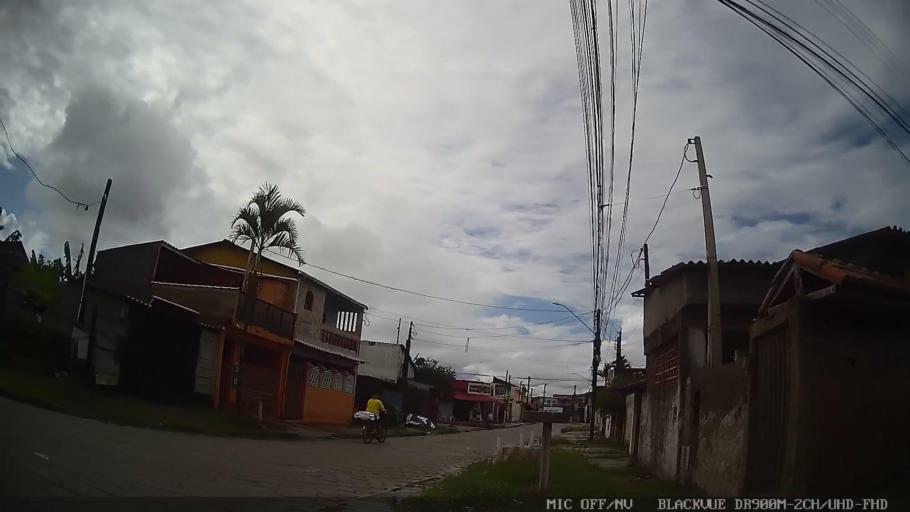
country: BR
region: Sao Paulo
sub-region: Itanhaem
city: Itanhaem
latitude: -24.1733
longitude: -46.7825
